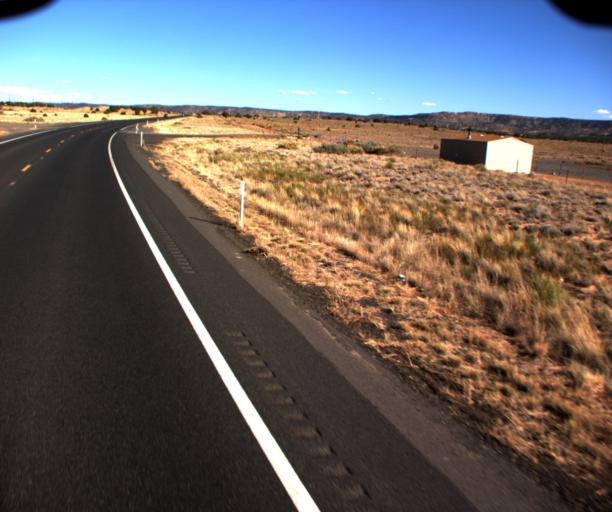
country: US
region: Arizona
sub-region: Coconino County
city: Kaibito
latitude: 36.4405
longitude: -110.7493
